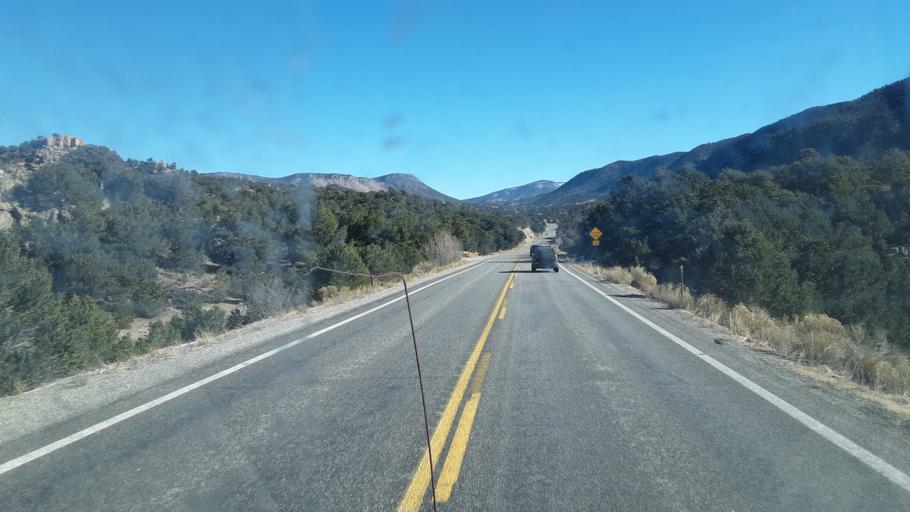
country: US
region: Colorado
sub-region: Chaffee County
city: Buena Vista
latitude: 38.8182
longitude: -106.0744
